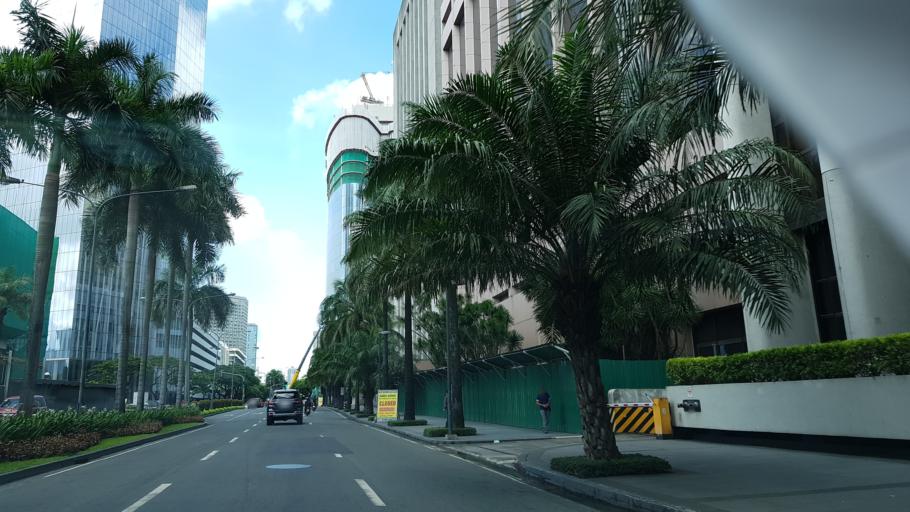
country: PH
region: Metro Manila
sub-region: Makati City
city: Makati City
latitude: 14.5599
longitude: 121.0270
